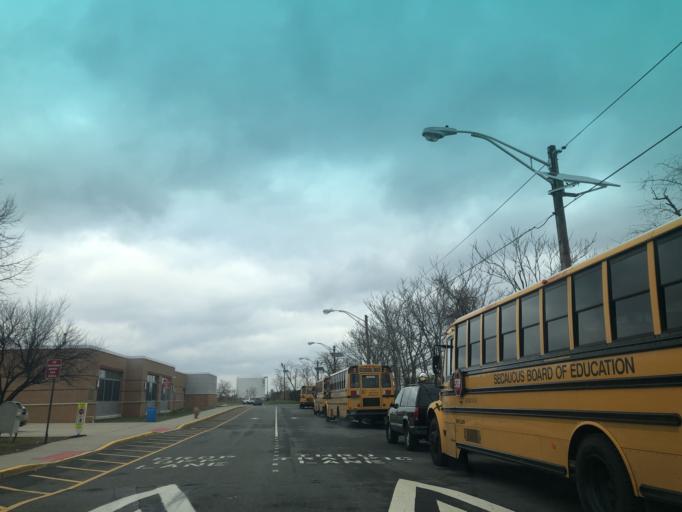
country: US
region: New Jersey
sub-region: Hudson County
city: Secaucus
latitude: 40.8037
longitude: -74.0503
